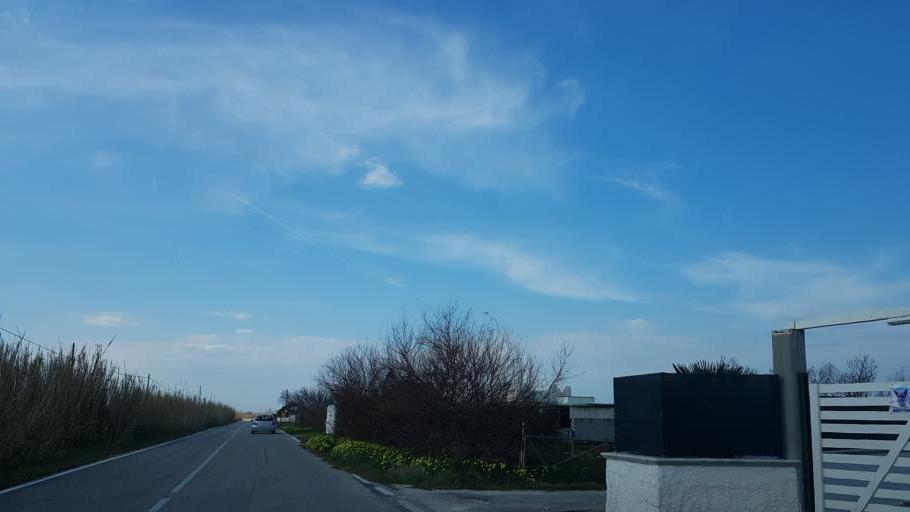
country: IT
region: Apulia
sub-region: Provincia di Brindisi
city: Brindisi
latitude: 40.6829
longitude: 17.8854
